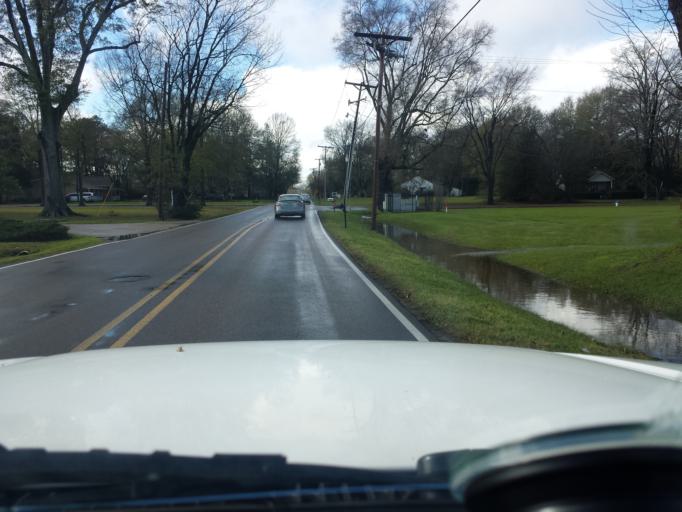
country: US
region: Mississippi
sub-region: Madison County
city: Madison
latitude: 32.4578
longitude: -90.1140
